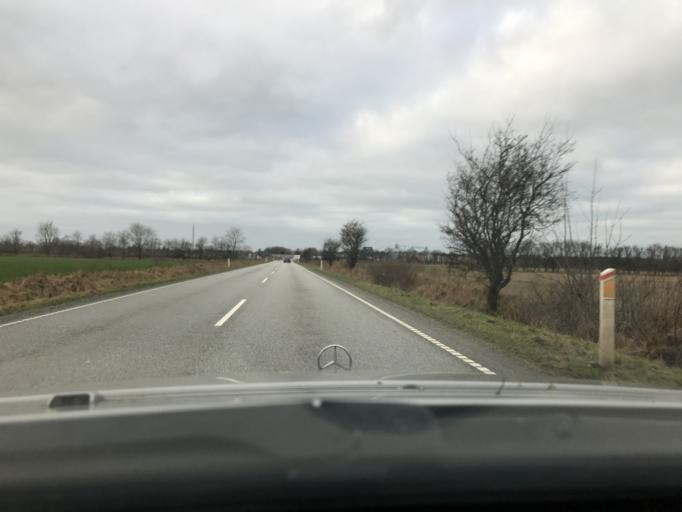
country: DK
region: South Denmark
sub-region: Aabenraa Kommune
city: Rodekro
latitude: 55.0764
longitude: 9.2303
